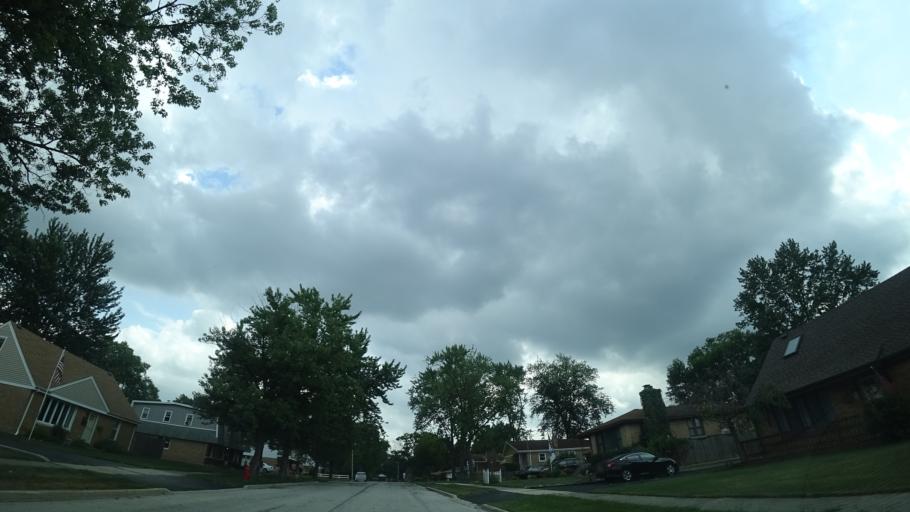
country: US
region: Illinois
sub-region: Cook County
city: Chicago Ridge
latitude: 41.6967
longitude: -87.7655
